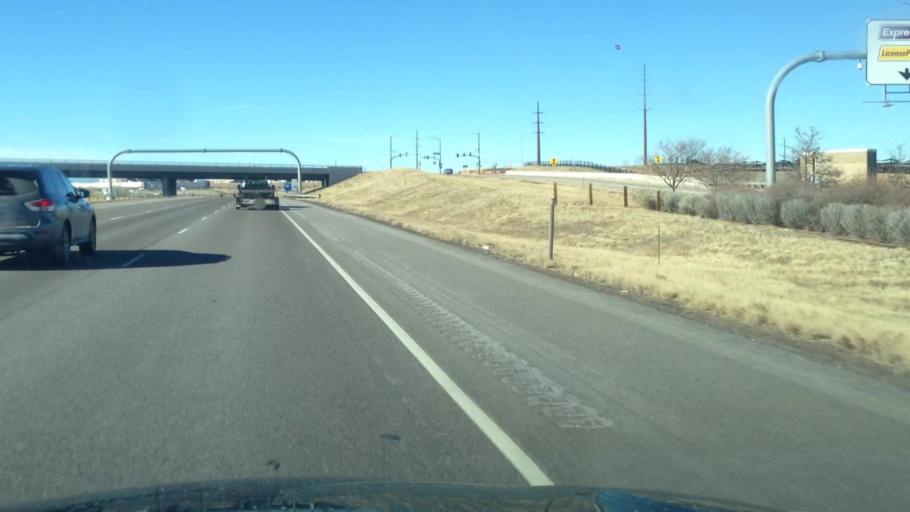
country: US
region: Colorado
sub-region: Douglas County
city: Stonegate
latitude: 39.5518
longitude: -104.8052
